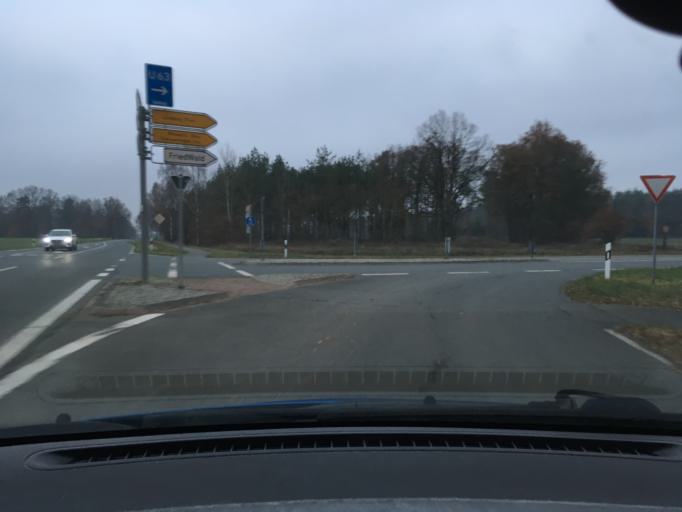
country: DE
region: Lower Saxony
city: Bispingen
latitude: 53.1208
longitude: 9.9505
